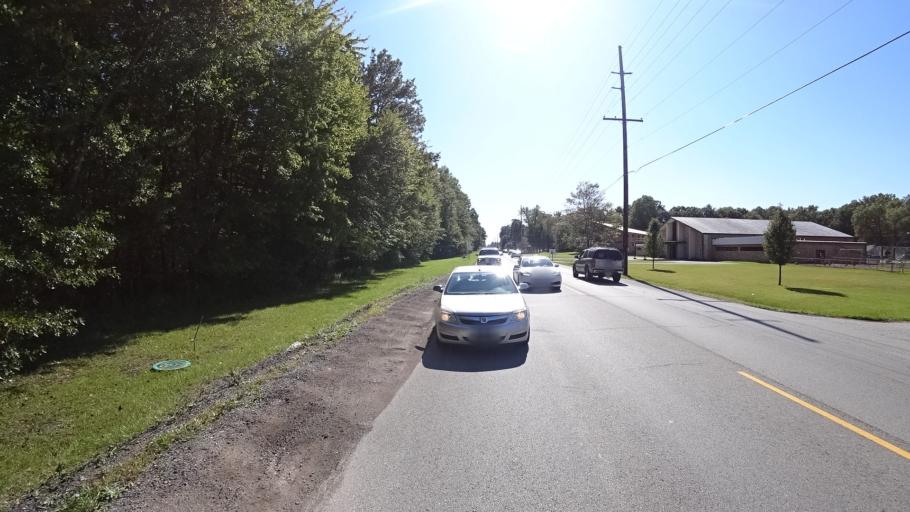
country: US
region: Indiana
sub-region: LaPorte County
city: Trail Creek
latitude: 41.6929
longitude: -86.8744
